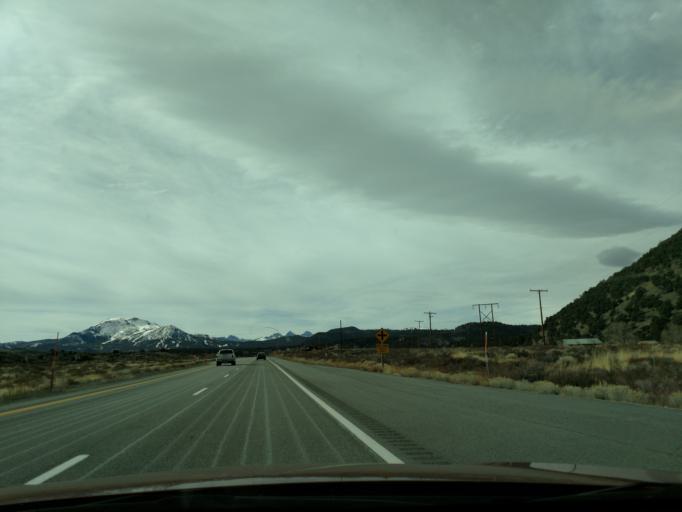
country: US
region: California
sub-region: Mono County
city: Mammoth Lakes
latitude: 37.6365
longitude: -118.8911
